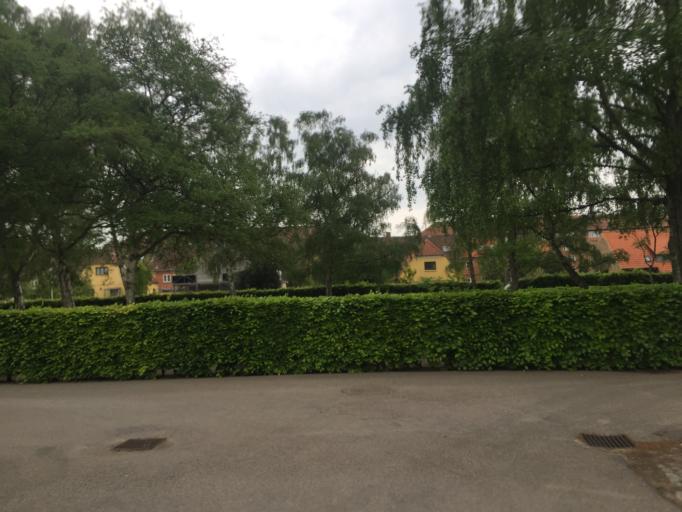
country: DK
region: Capital Region
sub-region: Kobenhavn
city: Vanlose
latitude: 55.6702
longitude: 12.5081
